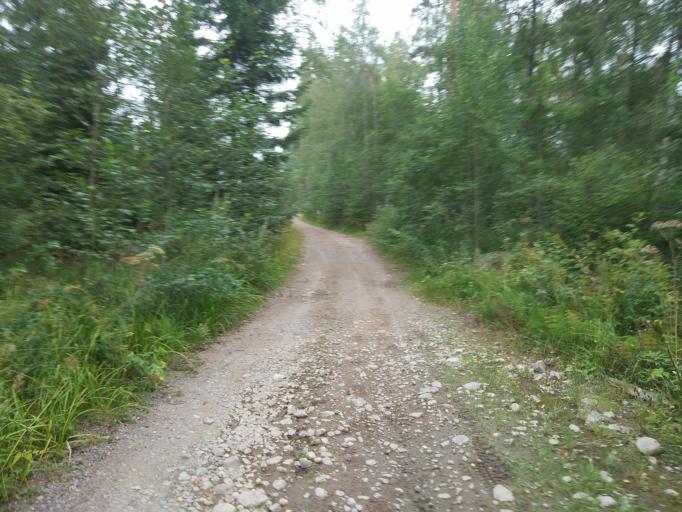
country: RU
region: Leningrad
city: Kuznechnoye
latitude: 61.1195
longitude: 29.5974
